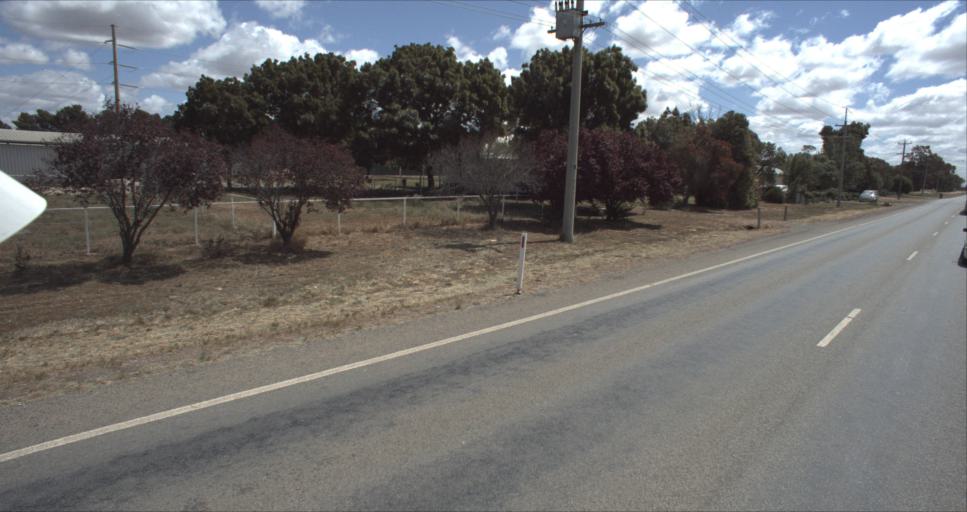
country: AU
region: New South Wales
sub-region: Murrumbidgee Shire
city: Darlington Point
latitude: -34.5121
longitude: 146.1861
